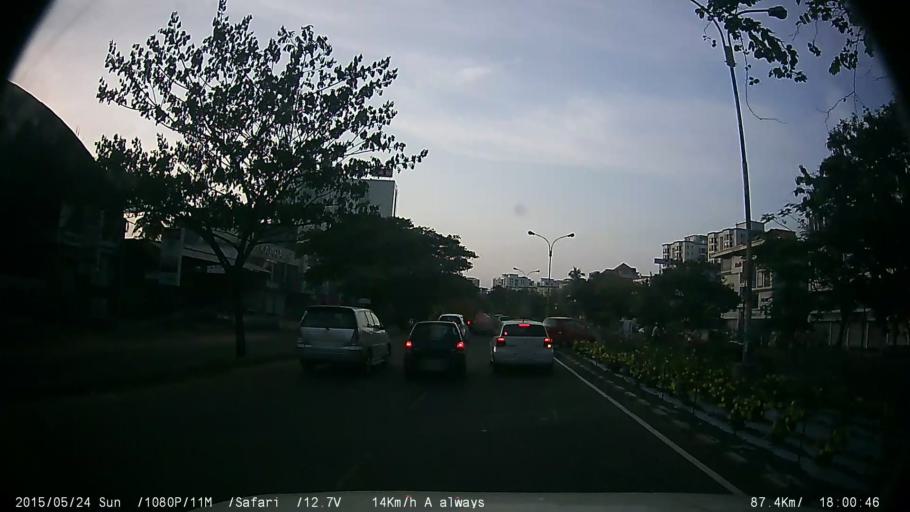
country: IN
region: Kerala
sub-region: Ernakulam
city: Elur
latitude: 10.0188
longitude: 76.3108
